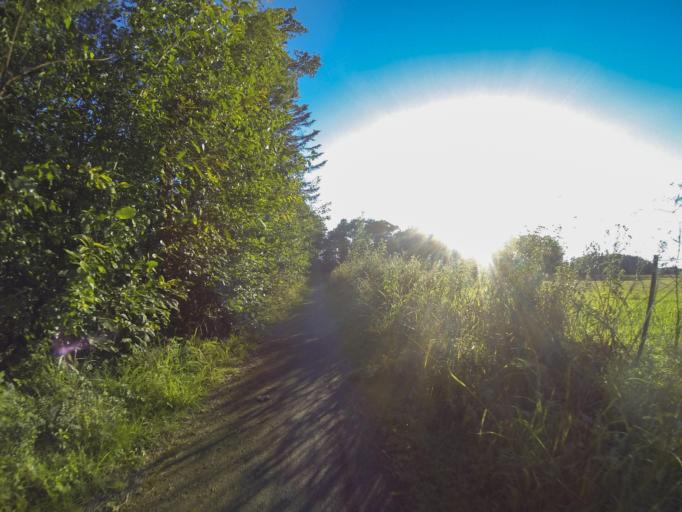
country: SE
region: Vaestmanland
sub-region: Vasteras
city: Vasteras
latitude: 59.5555
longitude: 16.6536
